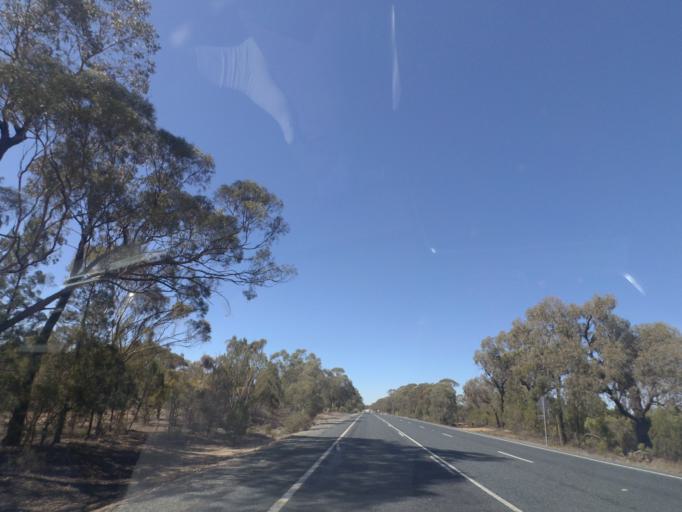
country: AU
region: New South Wales
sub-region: Bland
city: West Wyalong
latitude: -34.1302
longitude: 147.1239
